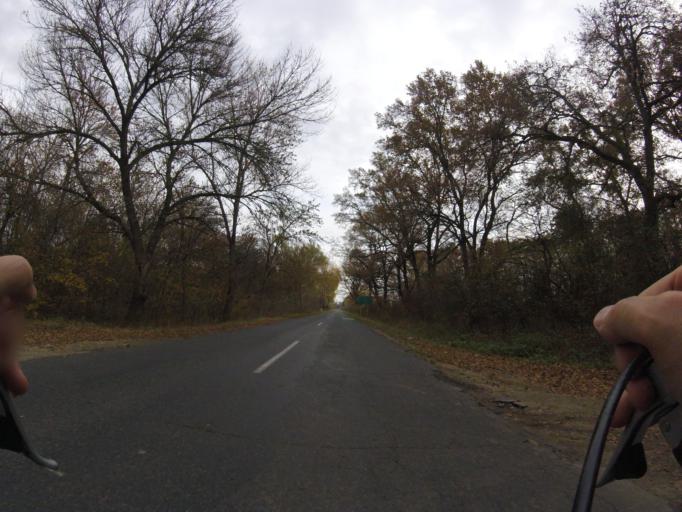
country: HU
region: Pest
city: Csemo
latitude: 47.0832
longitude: 19.6659
